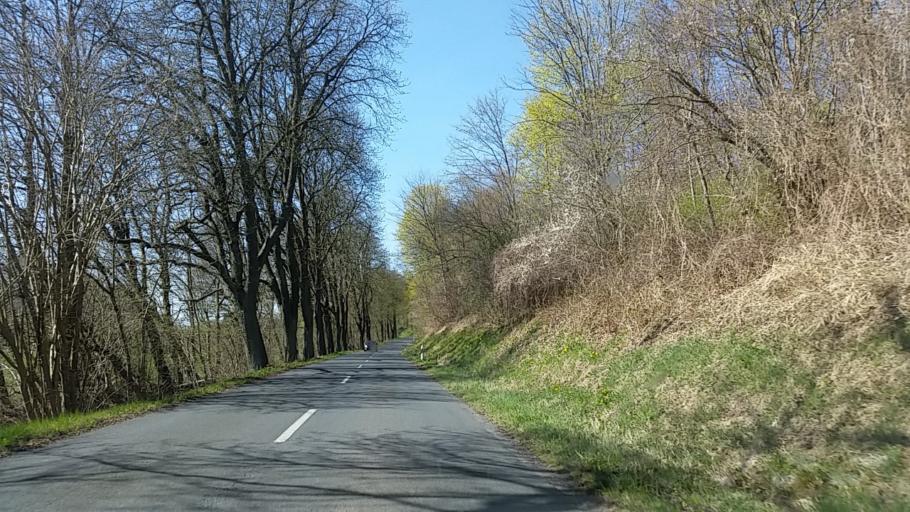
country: DE
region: Lower Saxony
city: Erkerode
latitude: 52.2067
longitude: 10.7256
